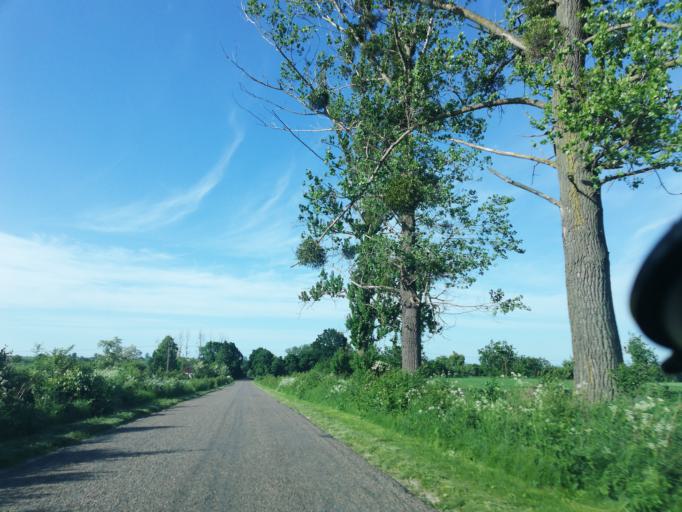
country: PL
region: Kujawsko-Pomorskie
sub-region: Powiat golubsko-dobrzynski
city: Golub-Dobrzyn
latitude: 53.0249
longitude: 19.0660
